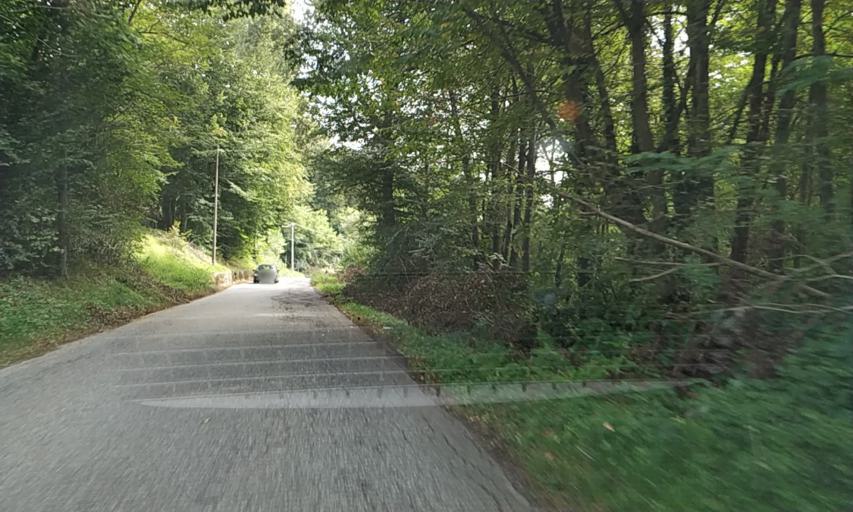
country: IT
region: Piedmont
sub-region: Provincia di Biella
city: Ailoche
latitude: 45.6884
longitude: 8.2238
